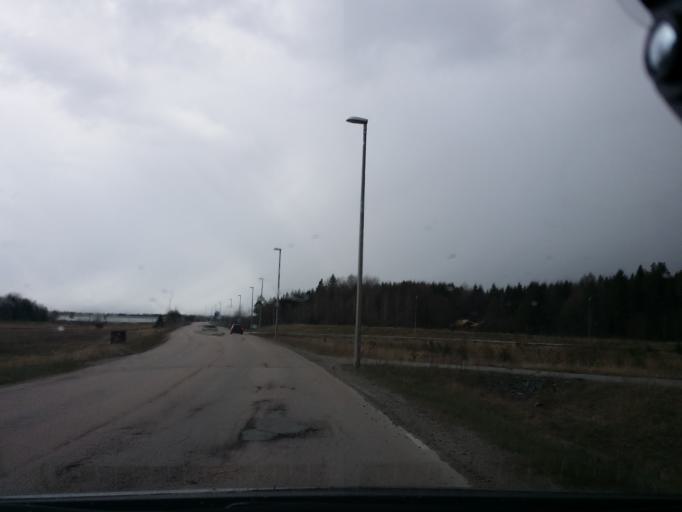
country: SE
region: Uppsala
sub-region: Enkopings Kommun
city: Enkoping
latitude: 59.6431
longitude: 17.1448
